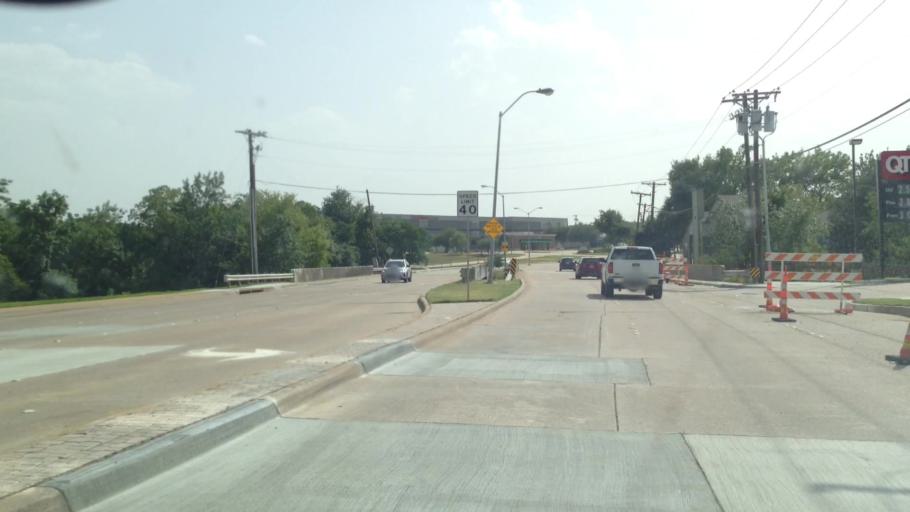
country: US
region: Texas
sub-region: Collin County
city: Plano
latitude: 33.0279
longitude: -96.7129
